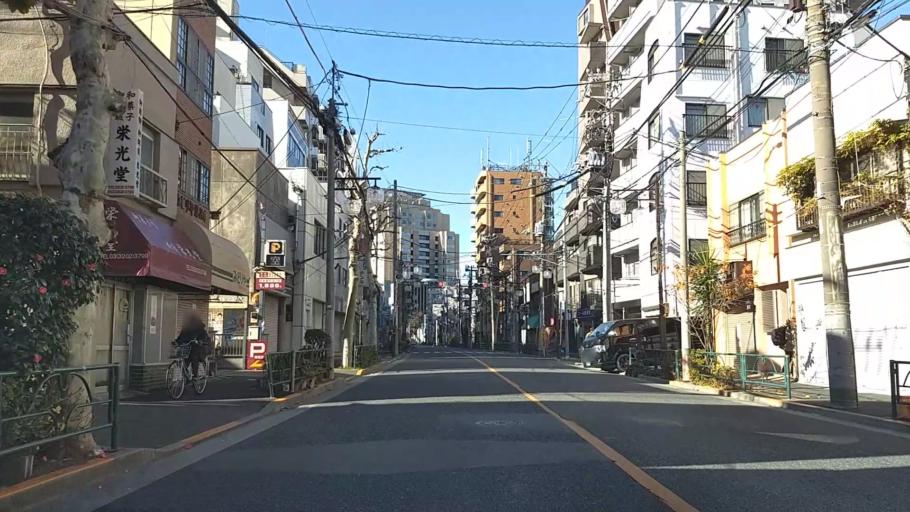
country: JP
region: Tokyo
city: Tokyo
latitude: 35.7005
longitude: 139.7201
